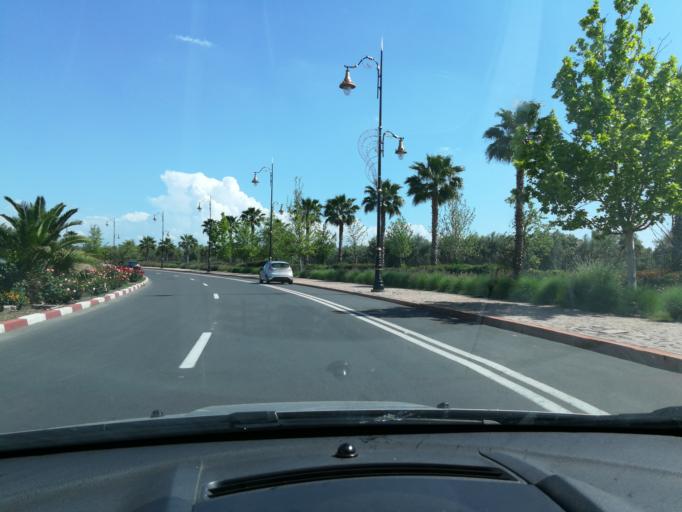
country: MA
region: Marrakech-Tensift-Al Haouz
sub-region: Marrakech
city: Marrakesh
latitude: 31.6136
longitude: -8.0072
